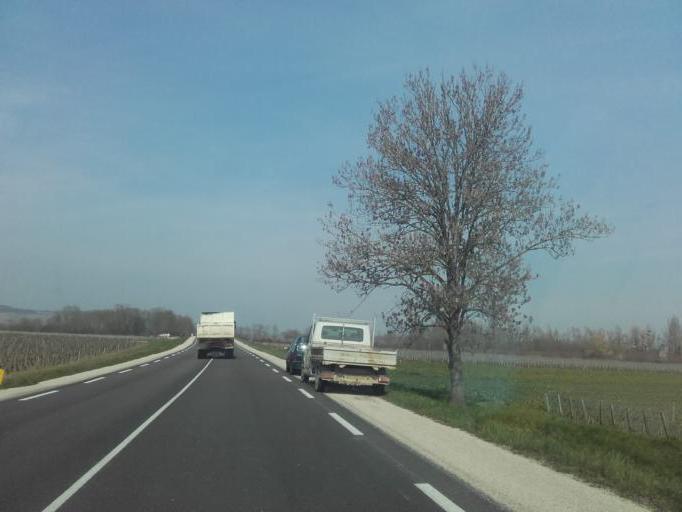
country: FR
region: Bourgogne
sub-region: Departement de la Cote-d'Or
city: Meursault
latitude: 46.9845
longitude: 4.7911
